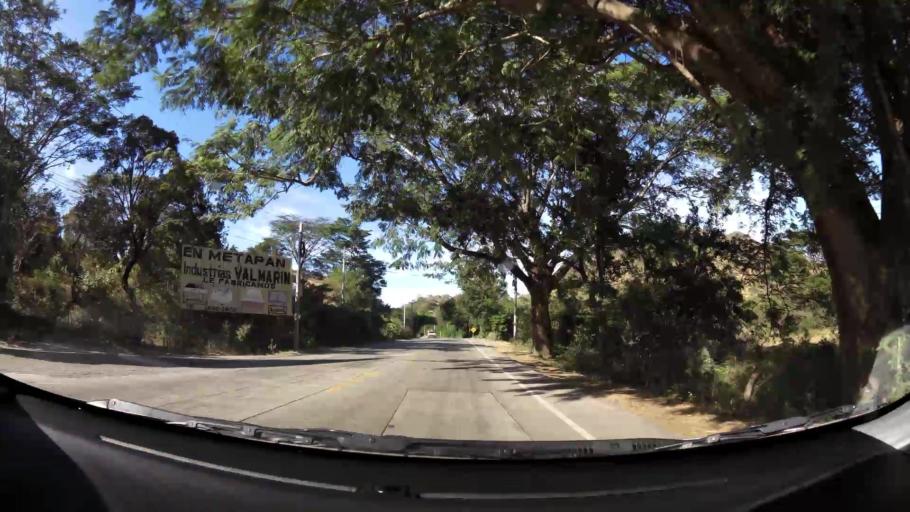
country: SV
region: Santa Ana
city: Texistepeque
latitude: 14.1095
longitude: -89.4990
